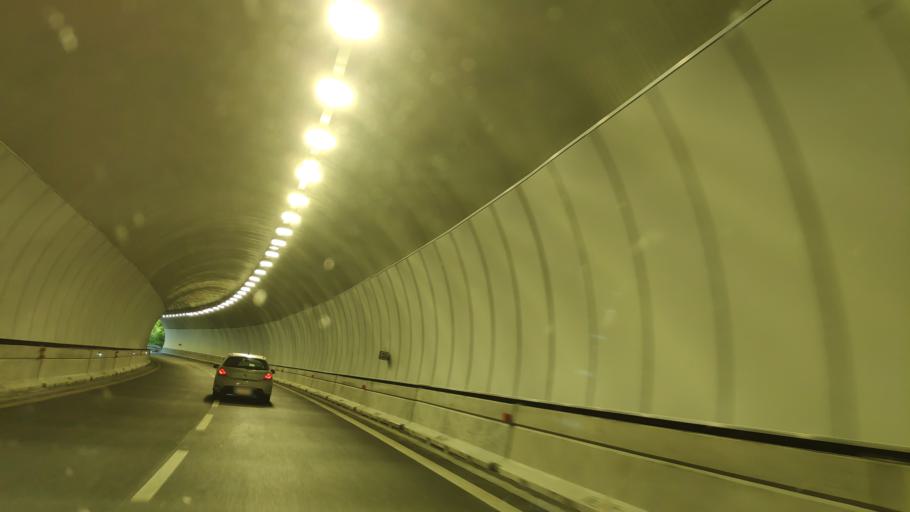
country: IT
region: Calabria
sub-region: Provincia di Cosenza
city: Carpanzano
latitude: 39.1559
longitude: 16.2884
